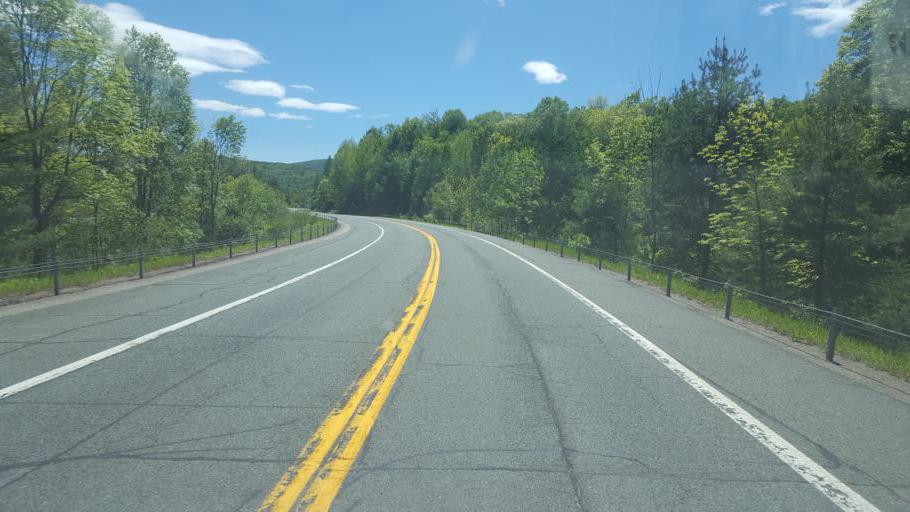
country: US
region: New York
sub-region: Hamilton County
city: Lake Pleasant
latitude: 43.3206
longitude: -74.5415
